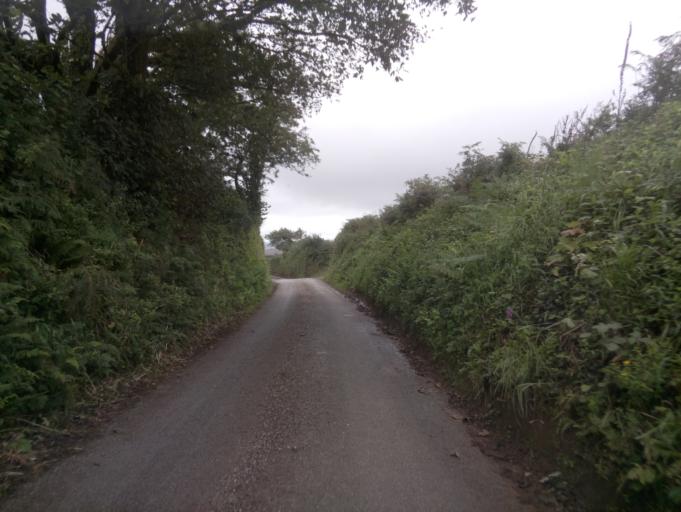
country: GB
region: England
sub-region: Devon
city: Kingsbridge
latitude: 50.2957
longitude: -3.7168
